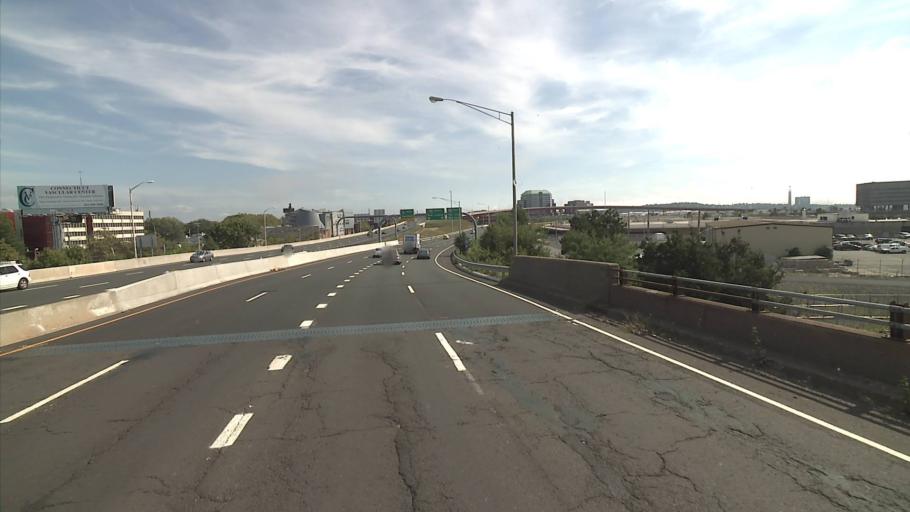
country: US
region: Connecticut
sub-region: New Haven County
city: New Haven
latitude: 41.3010
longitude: -72.9222
